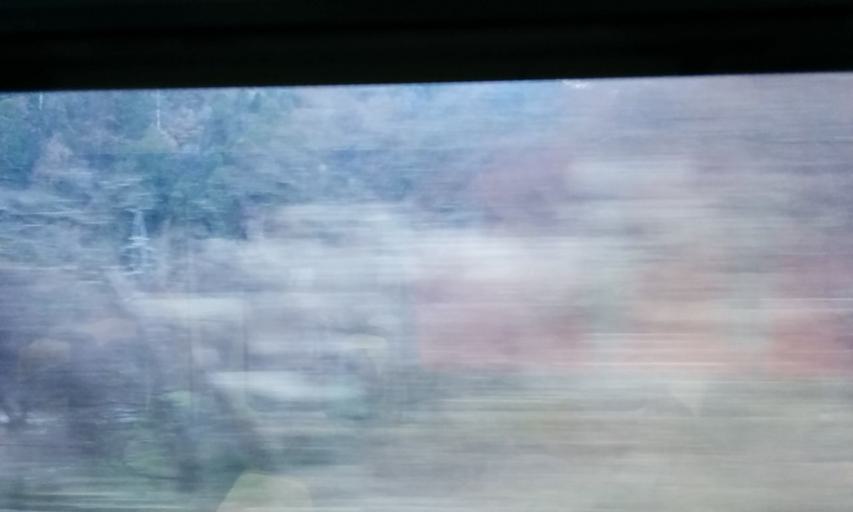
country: JP
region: Gifu
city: Nakatsugawa
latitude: 35.6579
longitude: 137.6211
